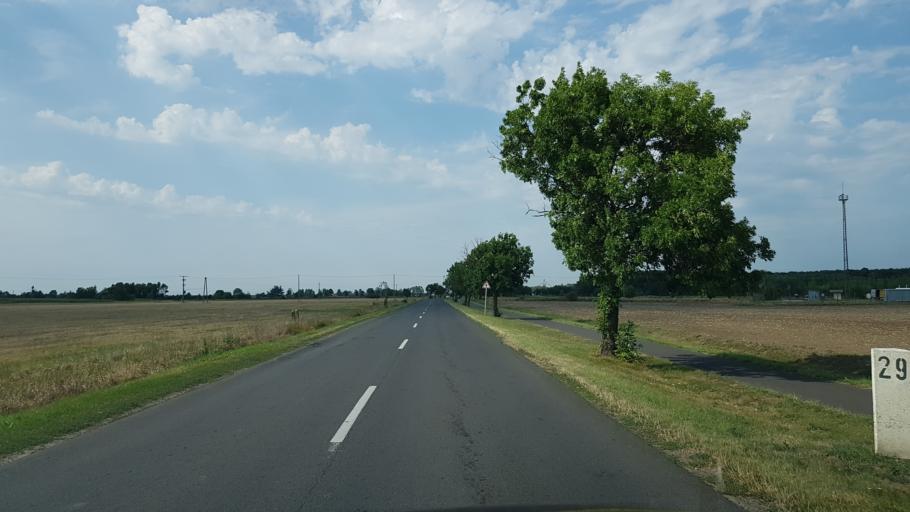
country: HU
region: Bekes
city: Fuzesgyarmat
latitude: 47.0712
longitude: 21.1963
